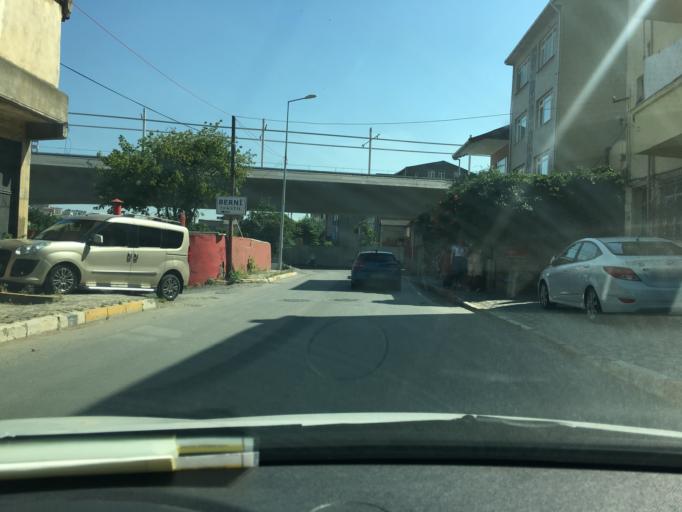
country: TR
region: Istanbul
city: Sisli
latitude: 41.0798
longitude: 28.9477
